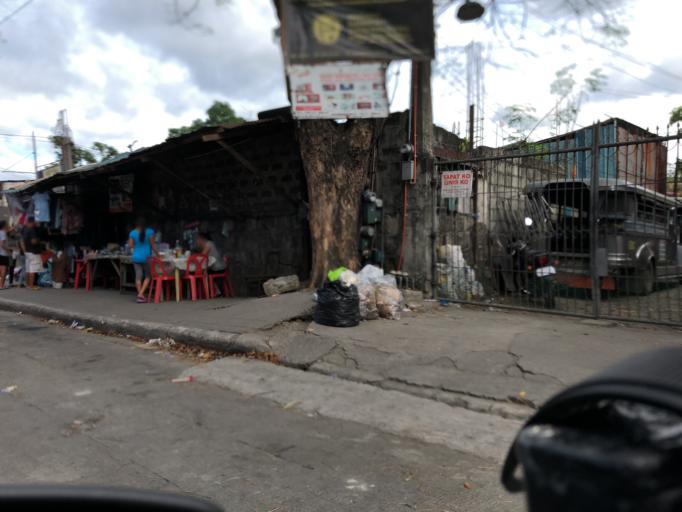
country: PH
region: Central Luzon
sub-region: Province of Bulacan
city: San Jose del Monte
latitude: 14.7416
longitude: 121.0562
